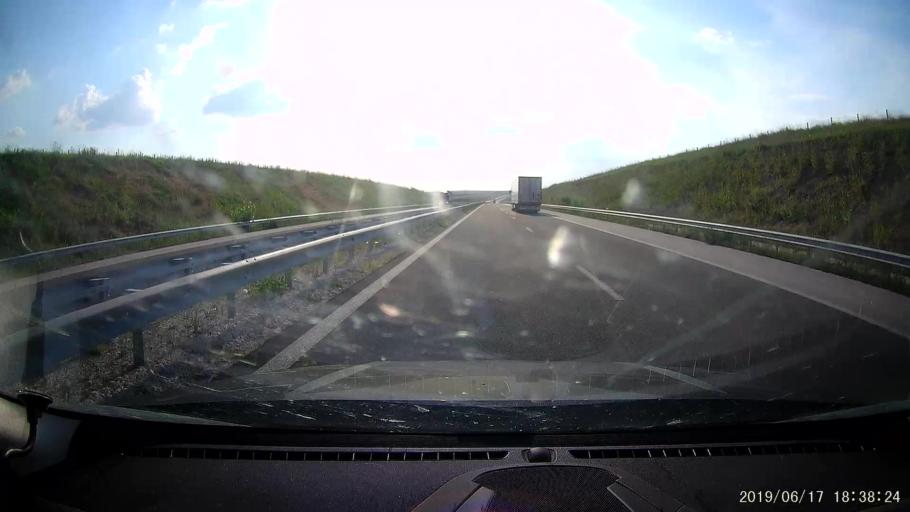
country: BG
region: Stara Zagora
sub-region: Obshtina Chirpan
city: Chirpan
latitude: 42.1367
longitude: 25.3380
